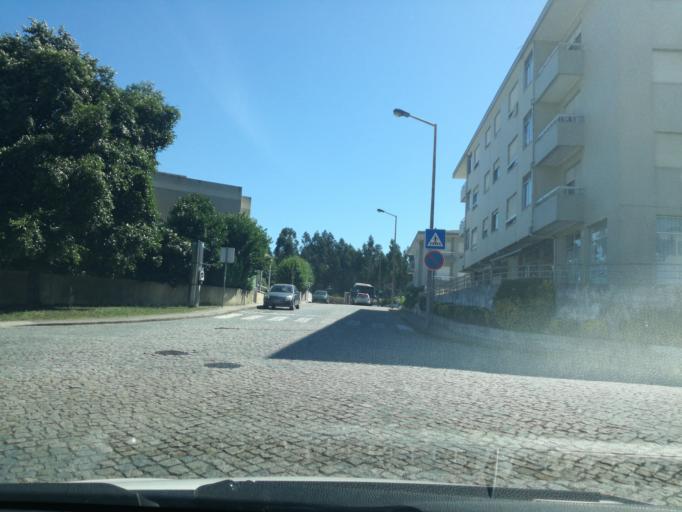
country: PT
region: Porto
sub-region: Maia
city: Maia
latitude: 41.2375
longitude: -8.6124
